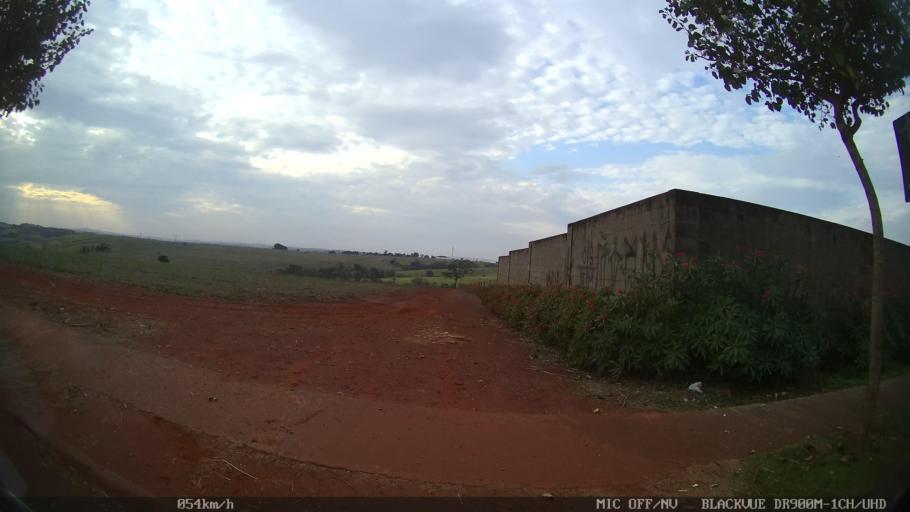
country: BR
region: Sao Paulo
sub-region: Americana
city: Americana
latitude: -22.6512
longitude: -47.3361
